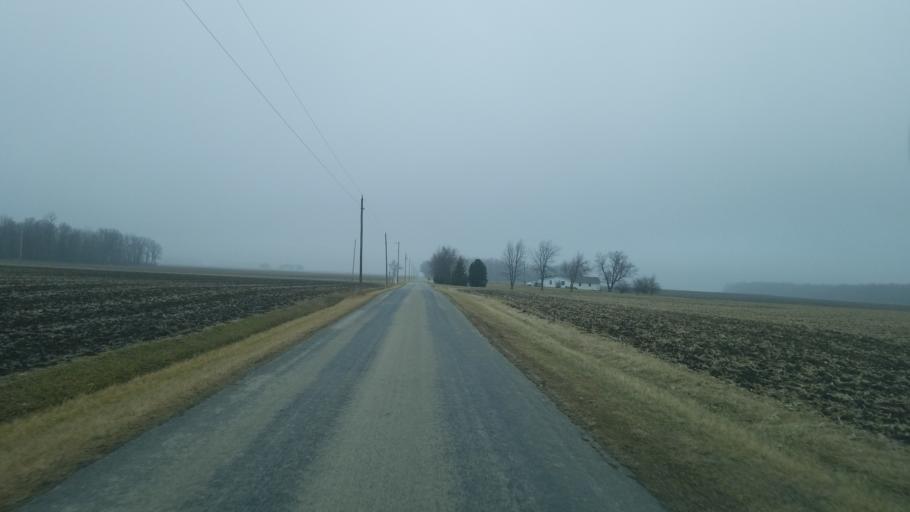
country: US
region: Indiana
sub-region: Adams County
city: Geneva
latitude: 40.5955
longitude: -85.1071
